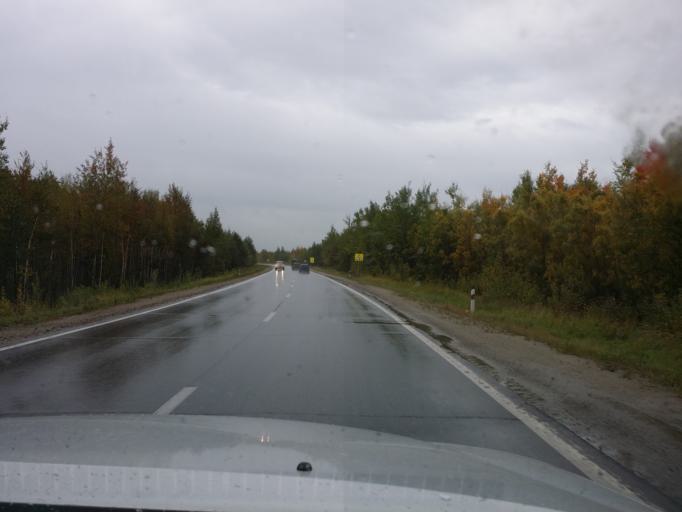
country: RU
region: Khanty-Mansiyskiy Avtonomnyy Okrug
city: Langepas
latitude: 61.1606
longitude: 75.5965
